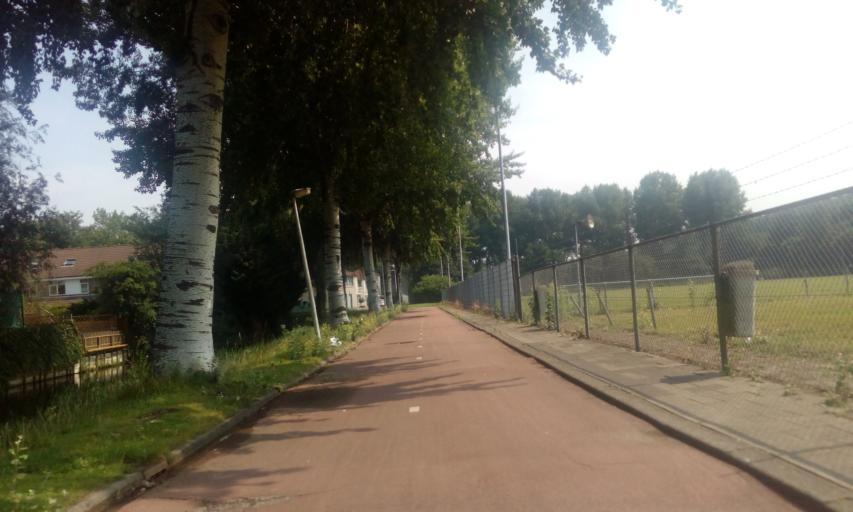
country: NL
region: South Holland
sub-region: Gemeente Capelle aan den IJssel
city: Capelle aan den IJssel
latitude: 51.9631
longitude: 4.5774
